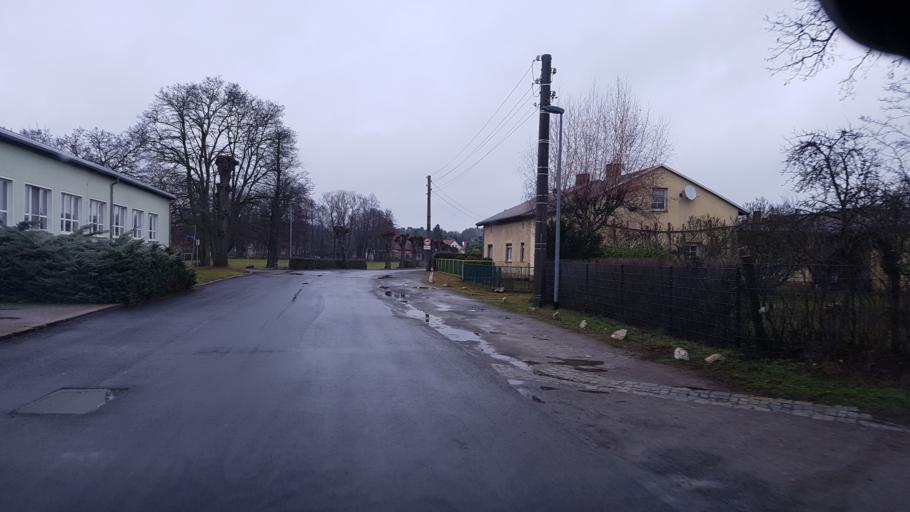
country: DE
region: Brandenburg
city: Bronkow
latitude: 51.6679
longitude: 13.9153
